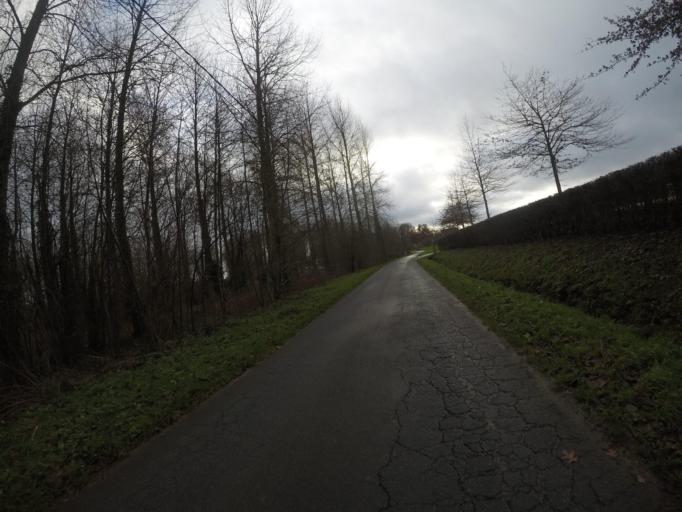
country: BE
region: Flanders
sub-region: Provincie Vlaams-Brabant
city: Gooik
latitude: 50.8055
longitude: 4.1247
